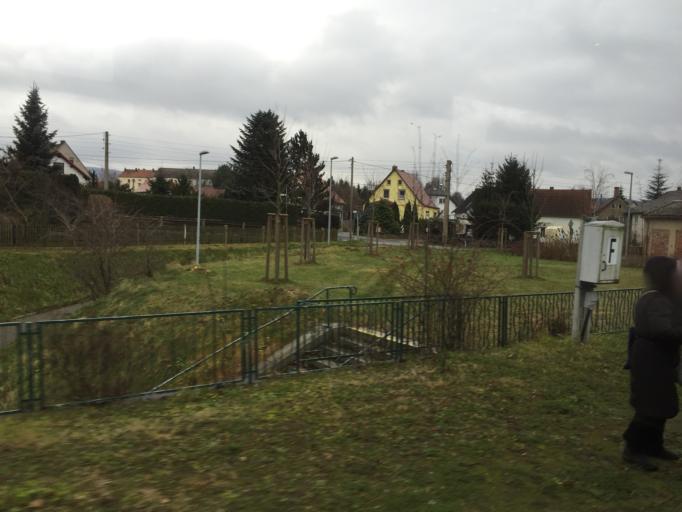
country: DE
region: Saxony
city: Kubschutz
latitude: 51.1656
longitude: 14.5091
